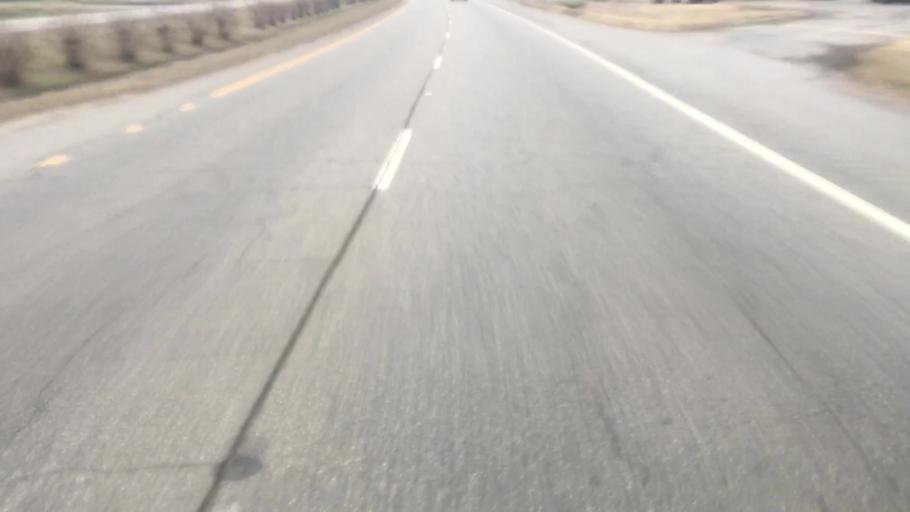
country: US
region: Alabama
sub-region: Walker County
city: Sumiton
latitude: 33.7415
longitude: -87.0385
